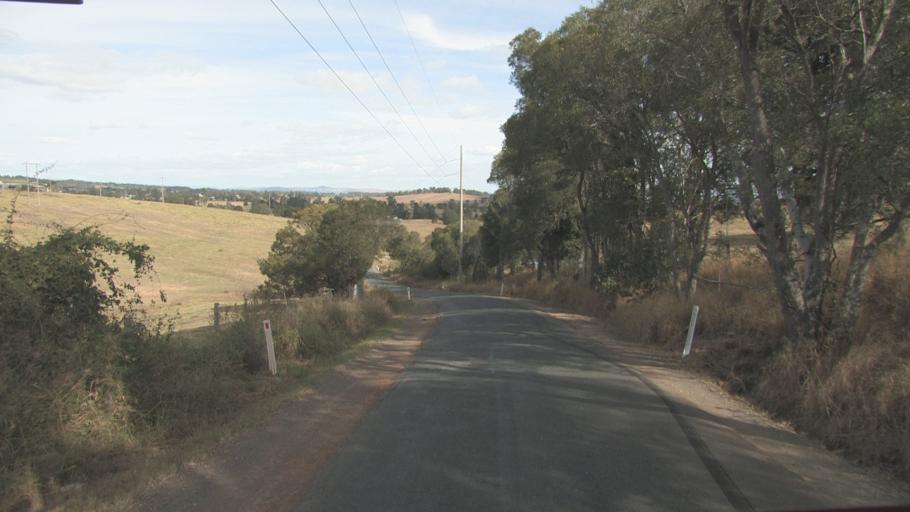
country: AU
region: Queensland
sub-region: Logan
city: Cedar Vale
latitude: -27.9062
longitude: 153.0138
